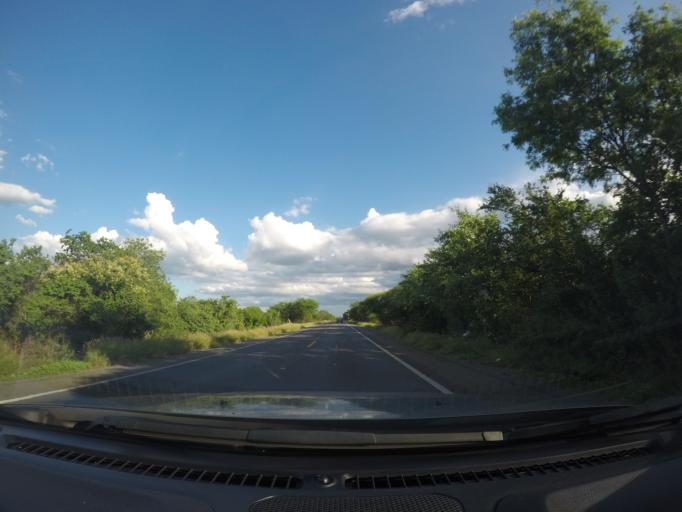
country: BR
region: Bahia
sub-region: Oliveira Dos Brejinhos
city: Beira Rio
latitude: -12.2240
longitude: -42.7883
